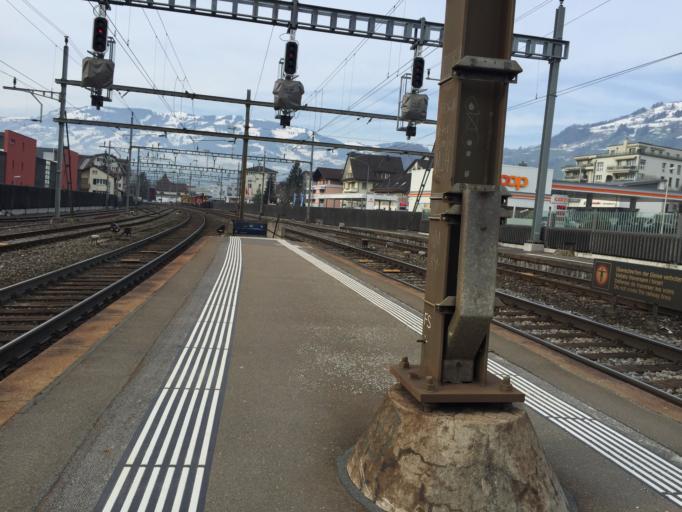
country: CH
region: Schwyz
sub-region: Bezirk Schwyz
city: Ibach
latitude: 47.0273
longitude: 8.6314
